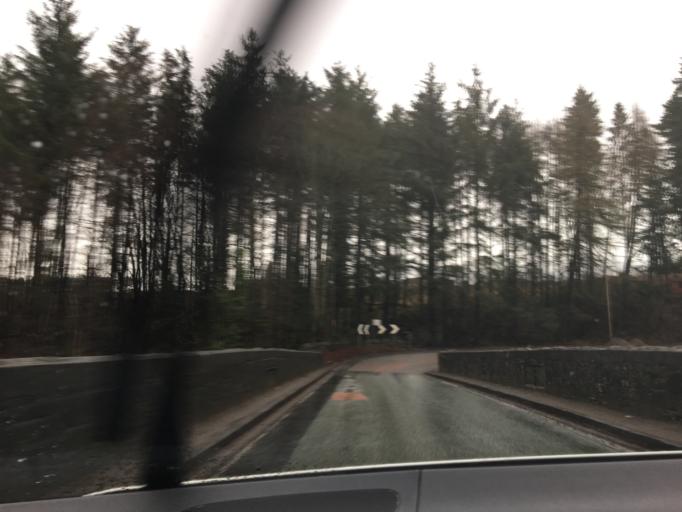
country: GB
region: Scotland
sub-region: Stirling
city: Doune
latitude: 56.1864
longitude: -4.0613
